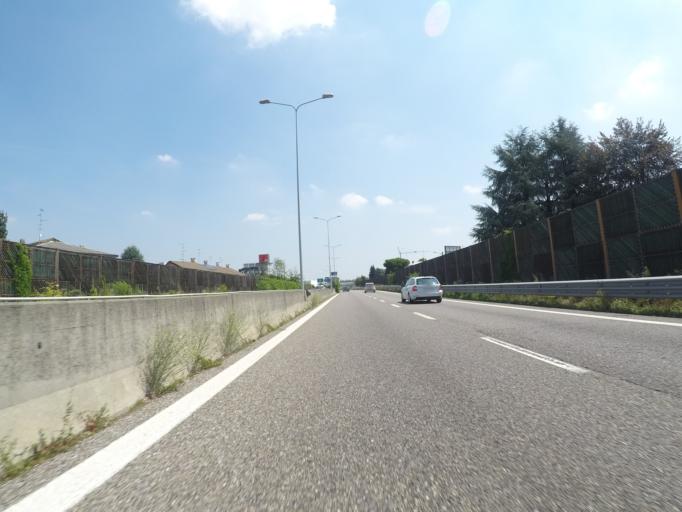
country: IT
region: Lombardy
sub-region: Provincia di Varese
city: Cardano al Campo
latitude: 45.6421
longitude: 8.7753
